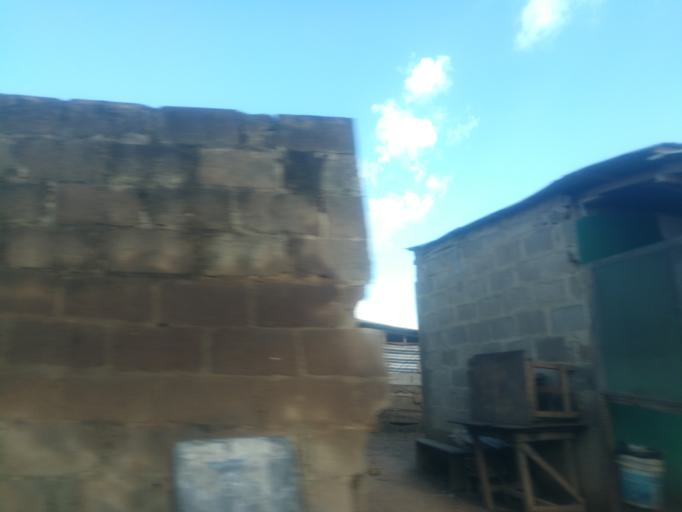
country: NG
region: Oyo
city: Lalupon
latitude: 7.4395
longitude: 3.9815
